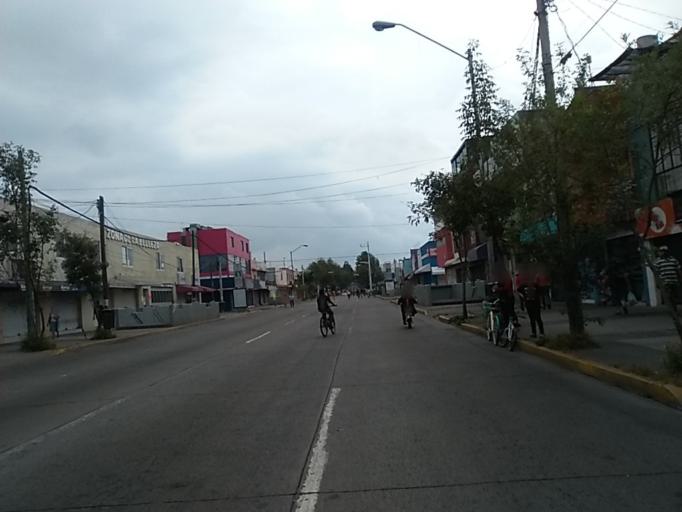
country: MX
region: Jalisco
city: Tlaquepaque
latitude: 20.6729
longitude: -103.3321
